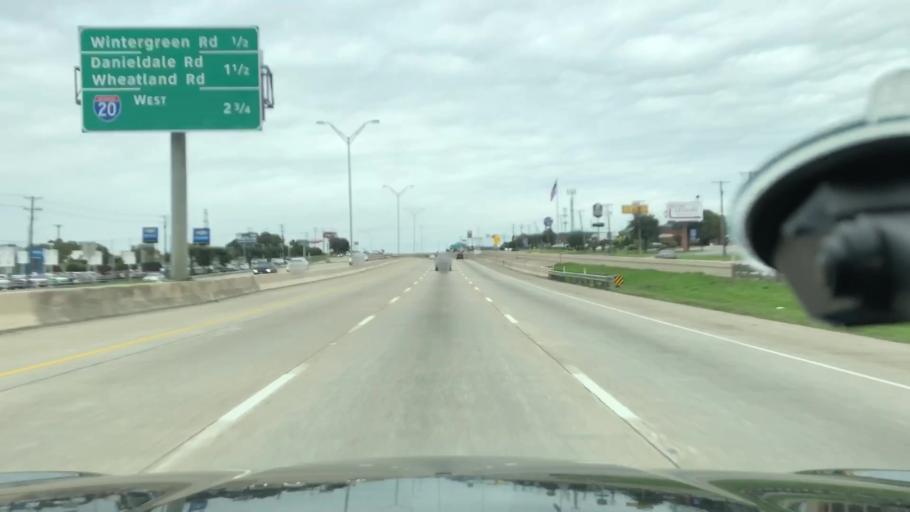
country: US
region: Texas
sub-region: Dallas County
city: DeSoto
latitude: 32.5976
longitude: -96.8224
